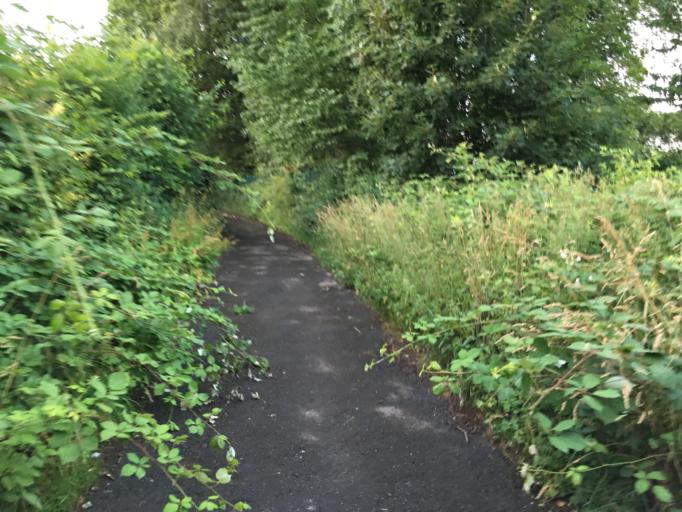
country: DE
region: North Rhine-Westphalia
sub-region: Regierungsbezirk Arnsberg
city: Frondenberg
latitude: 51.4797
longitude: 7.7248
